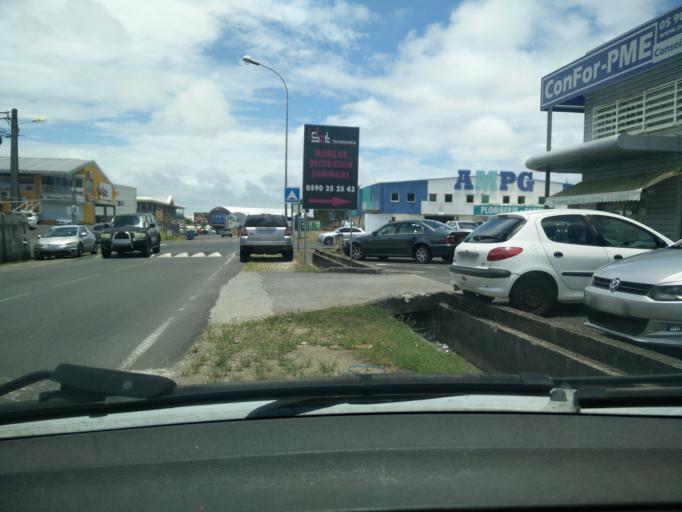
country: GP
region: Guadeloupe
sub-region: Guadeloupe
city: Pointe-a-Pitre
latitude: 16.2384
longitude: -61.5674
